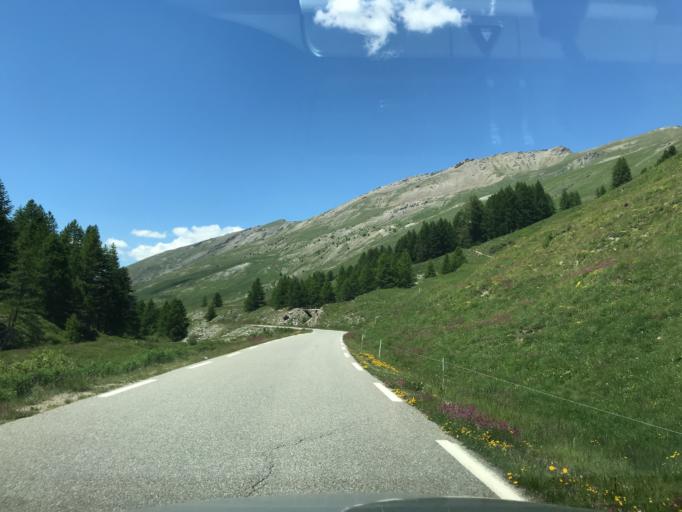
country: IT
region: Piedmont
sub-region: Provincia di Cuneo
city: Pontechianale
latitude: 44.7141
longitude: 6.9174
